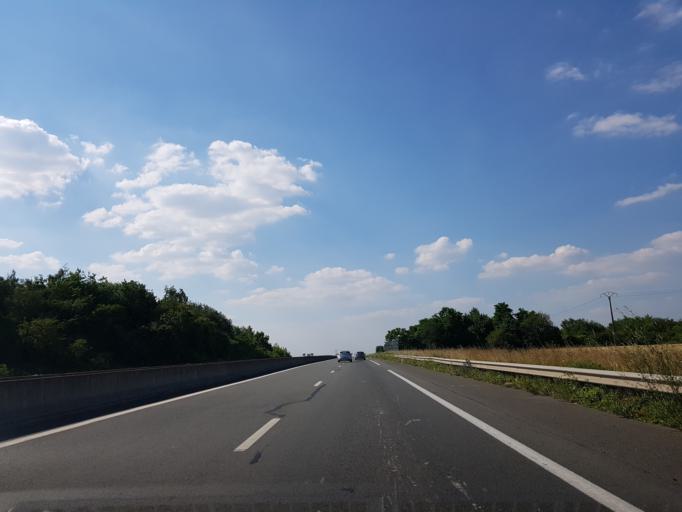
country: FR
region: Nord-Pas-de-Calais
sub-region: Departement du Nord
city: Abscon
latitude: 50.3367
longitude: 3.3204
